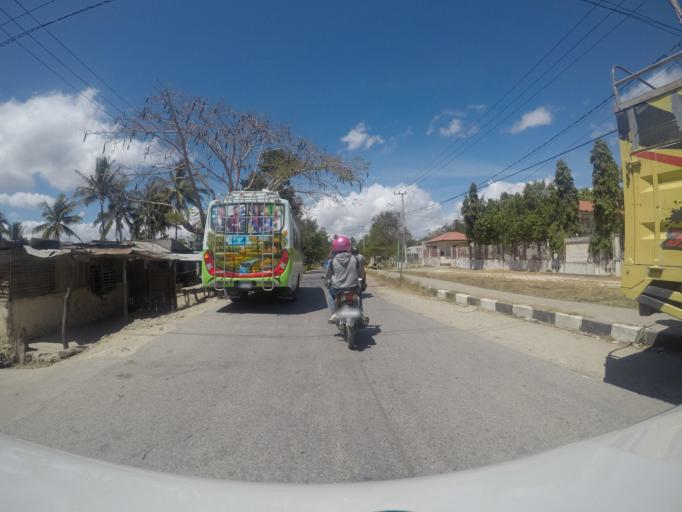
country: TL
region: Baucau
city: Baucau
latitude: -8.4764
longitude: 126.4584
